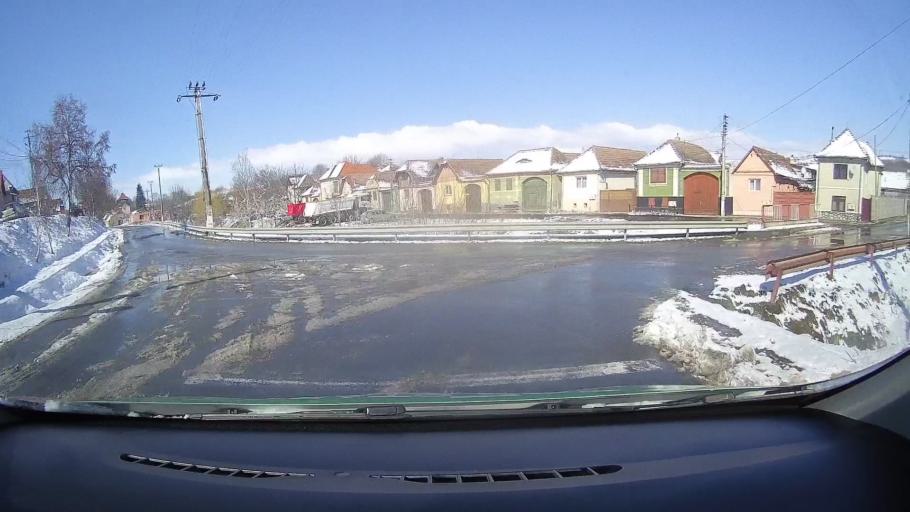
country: RO
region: Sibiu
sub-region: Comuna Rosia
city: Rosia
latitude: 45.8008
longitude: 24.2865
